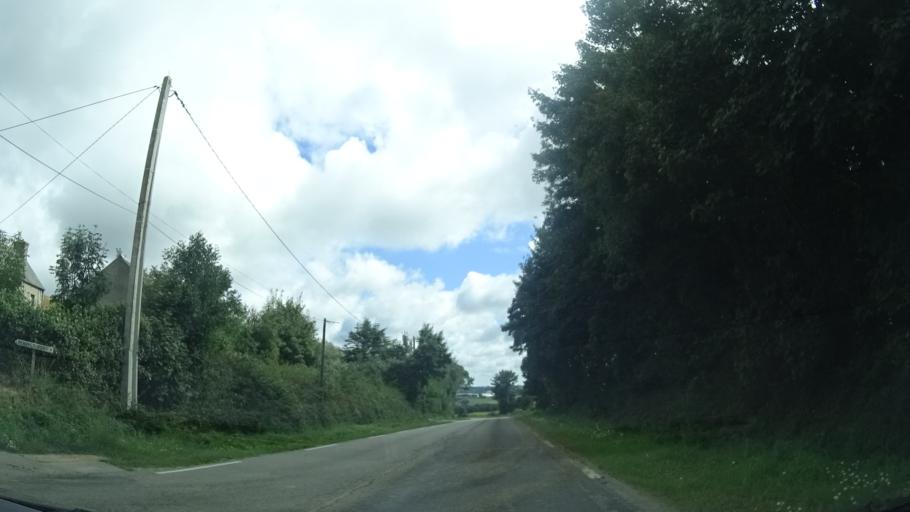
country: FR
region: Brittany
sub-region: Departement du Finistere
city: Lanrivoare
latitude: 48.4362
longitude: -4.6615
